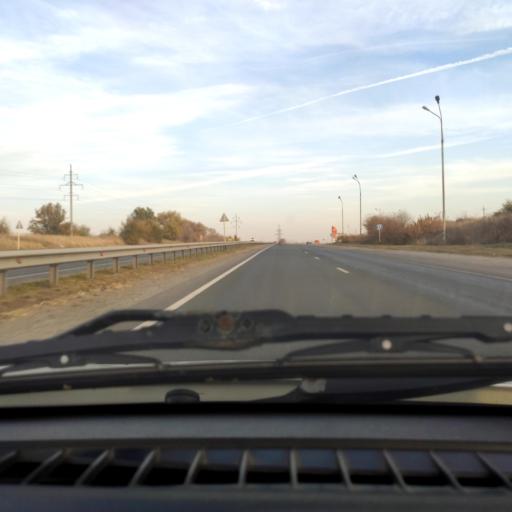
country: RU
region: Samara
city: Tol'yatti
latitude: 53.5682
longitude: 49.4860
